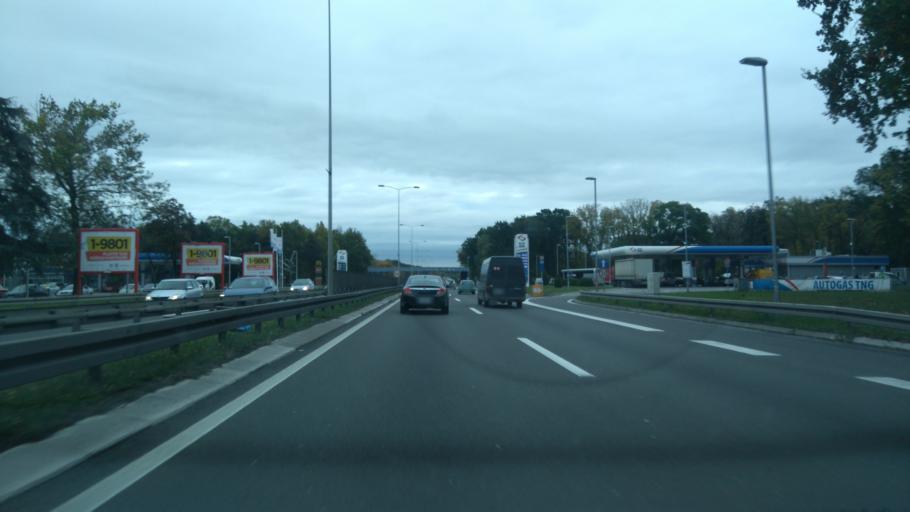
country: RS
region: Central Serbia
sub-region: Belgrade
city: Zemun
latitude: 44.8316
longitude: 20.3679
